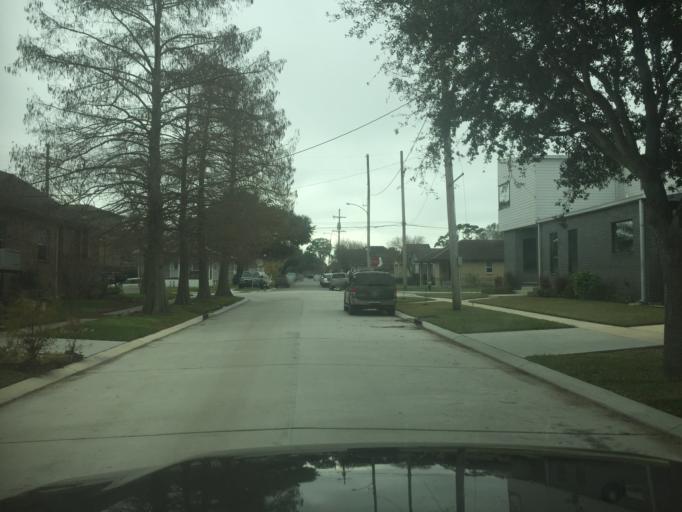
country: US
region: Louisiana
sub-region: Jefferson Parish
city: Metairie
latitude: 29.9999
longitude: -90.1110
